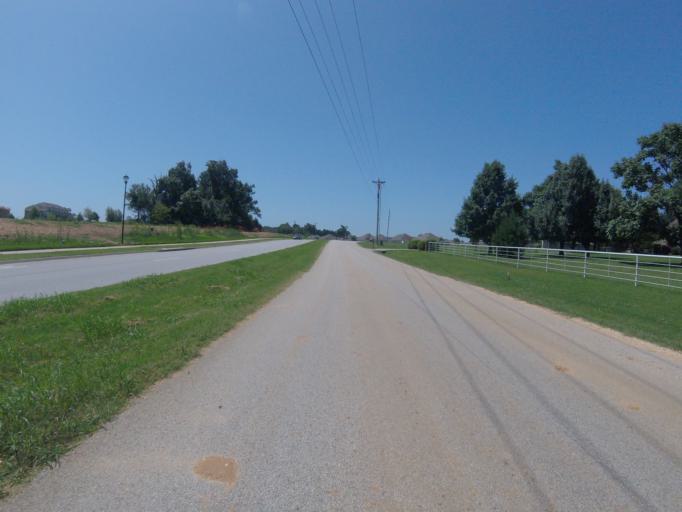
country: US
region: Arkansas
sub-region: Washington County
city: Farmington
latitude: 36.0870
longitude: -94.2166
